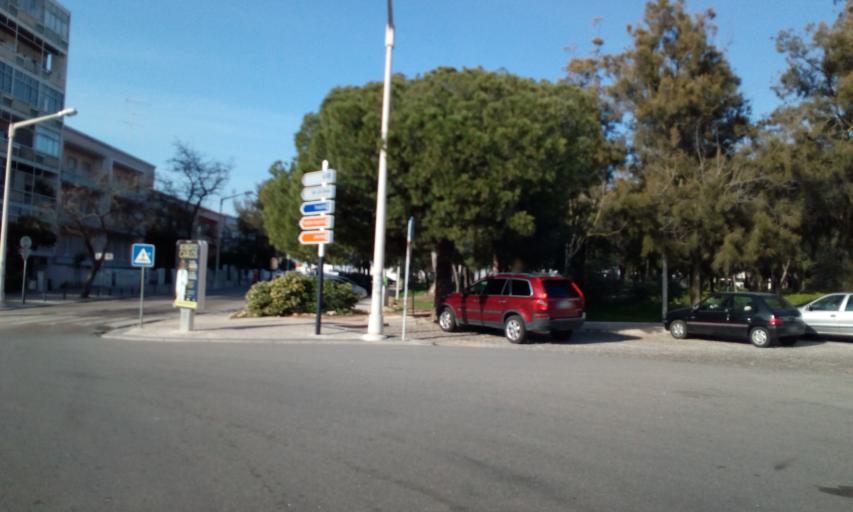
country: PT
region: Faro
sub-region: Faro
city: Faro
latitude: 37.0186
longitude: -7.9227
